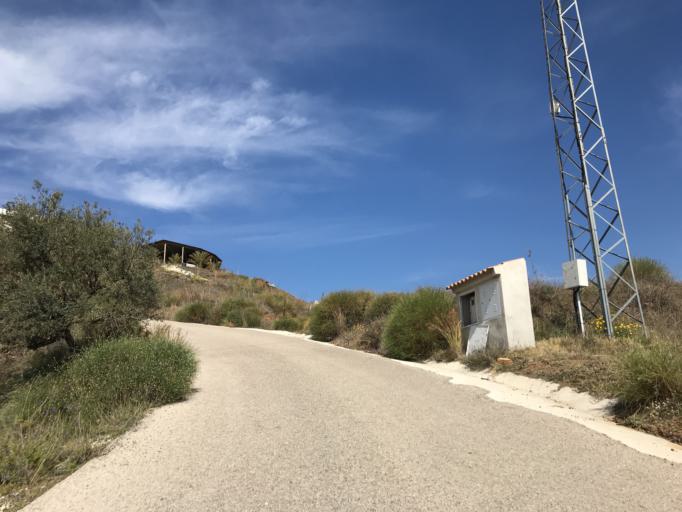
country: ES
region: Andalusia
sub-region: Provincia de Malaga
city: Valdes
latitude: 36.7733
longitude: -4.2151
